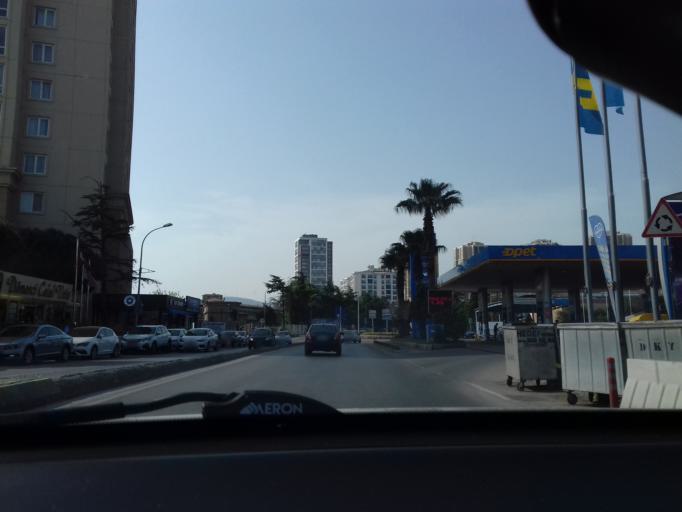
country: TR
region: Istanbul
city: Maltepe
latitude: 40.9099
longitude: 29.2117
